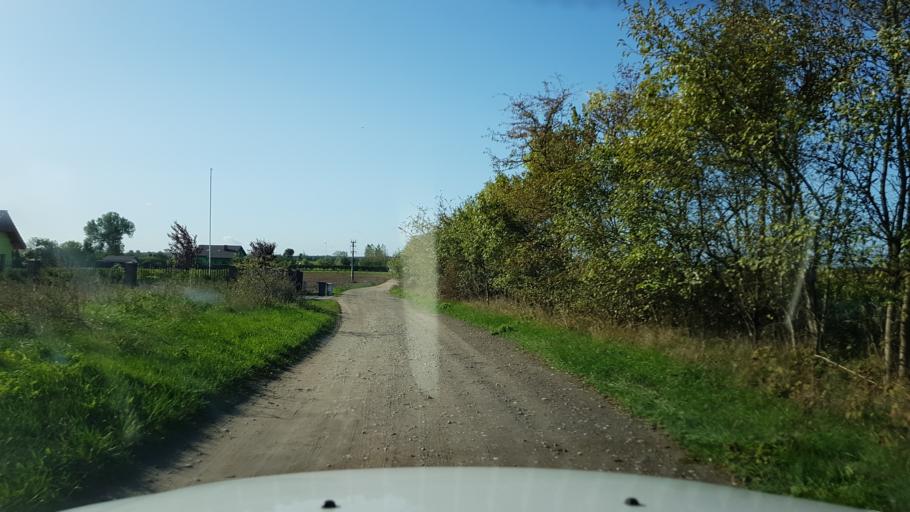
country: PL
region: West Pomeranian Voivodeship
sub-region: Powiat pyrzycki
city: Lipiany
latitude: 53.0143
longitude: 14.9328
